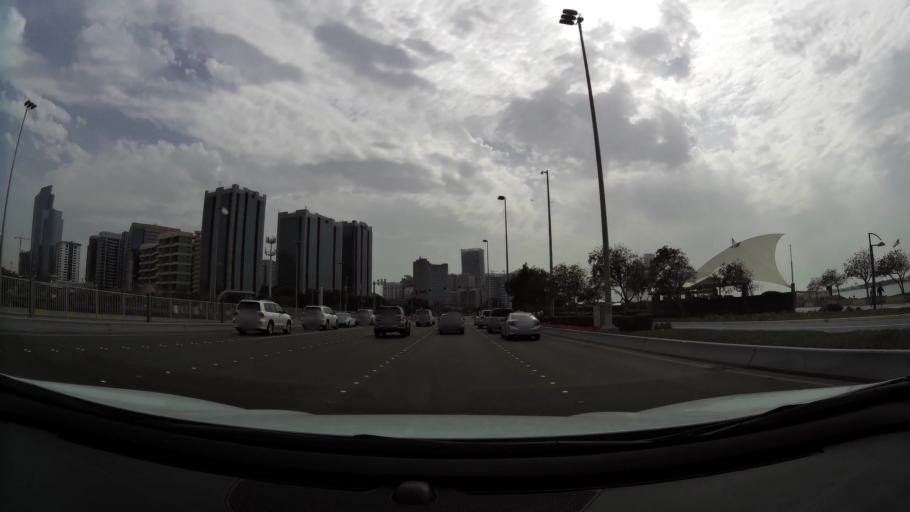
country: AE
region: Abu Dhabi
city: Abu Dhabi
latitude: 24.4790
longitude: 54.3457
